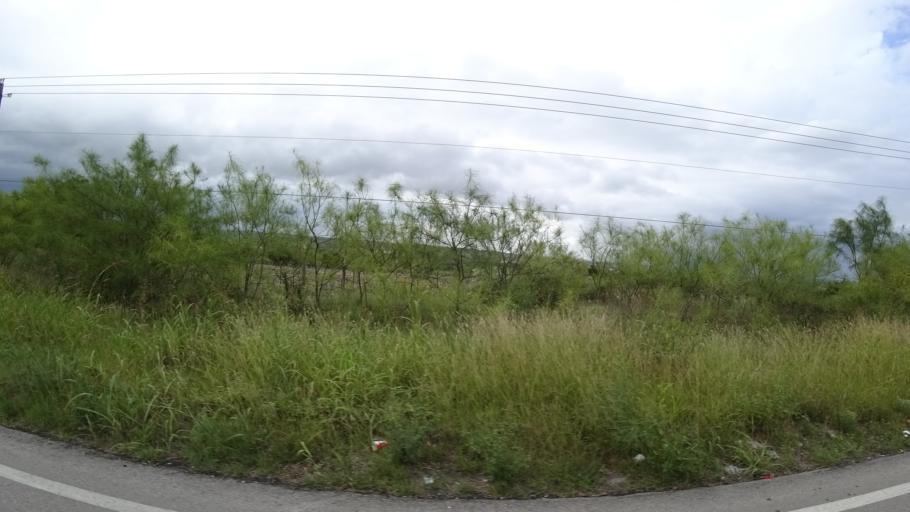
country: US
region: Texas
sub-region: Travis County
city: Onion Creek
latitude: 30.1493
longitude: -97.7312
